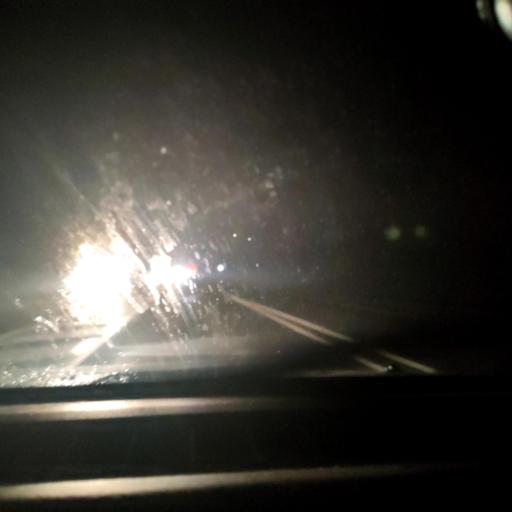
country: RU
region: Voronezj
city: Latnaya
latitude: 51.6415
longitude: 38.6959
